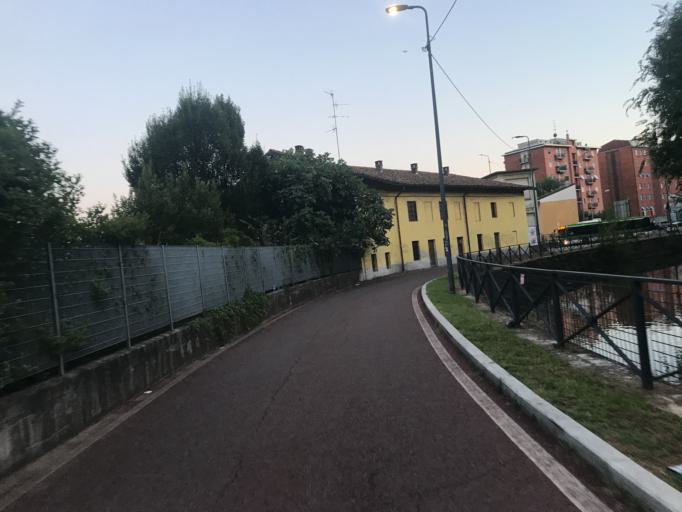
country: IT
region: Lombardy
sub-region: Citta metropolitana di Milano
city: Cologno Monzese
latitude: 45.5119
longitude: 9.2545
